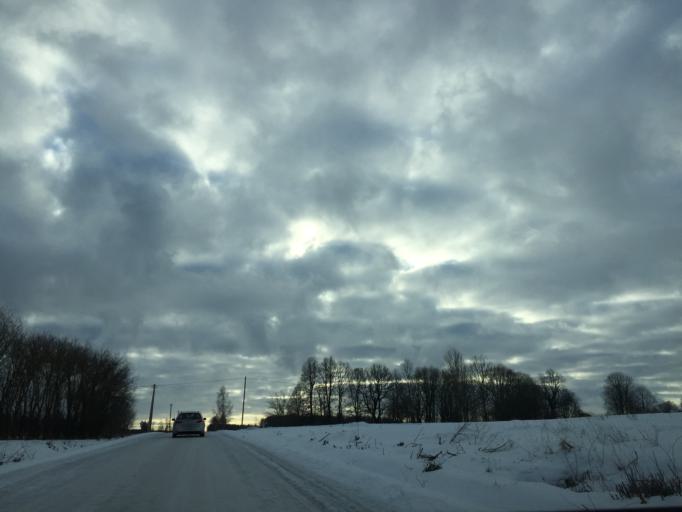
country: LV
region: Lielvarde
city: Lielvarde
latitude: 56.5603
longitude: 24.7353
